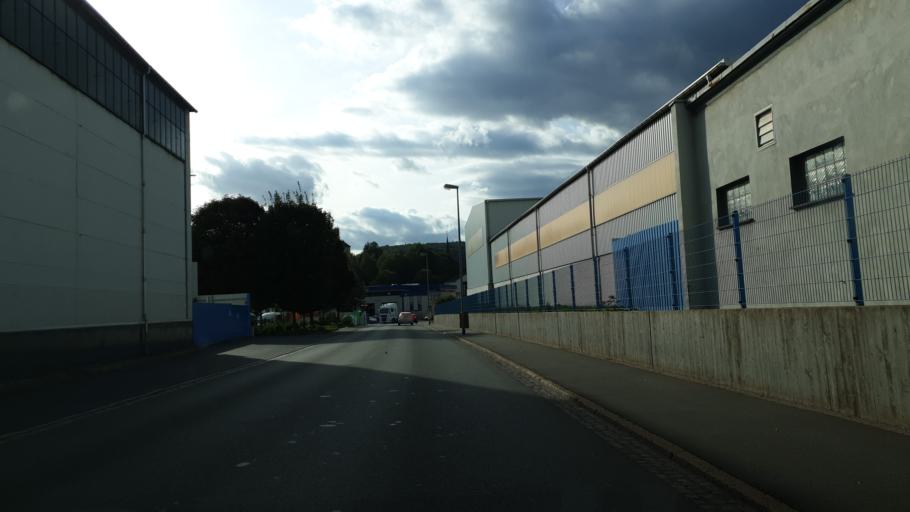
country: DE
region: Saxony
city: Aue
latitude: 50.5850
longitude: 12.7145
